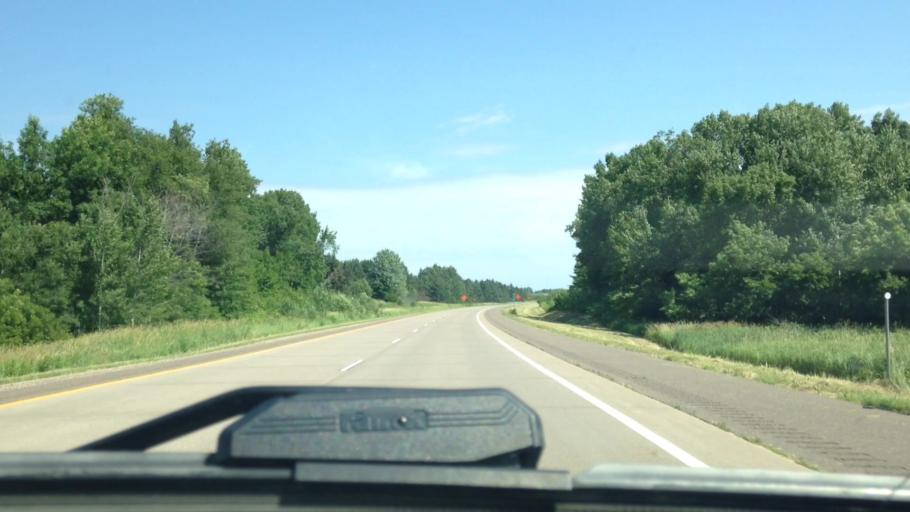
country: US
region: Wisconsin
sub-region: Barron County
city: Rice Lake
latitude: 45.5583
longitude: -91.7655
